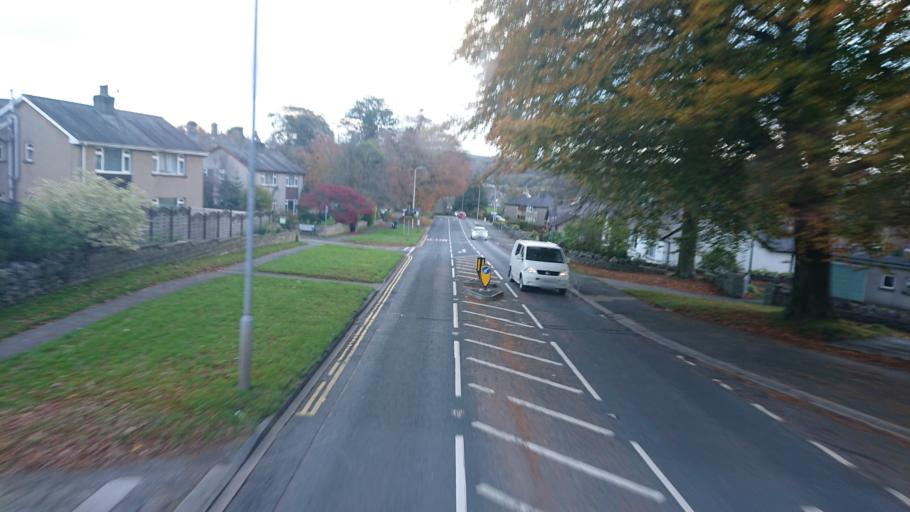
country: GB
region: England
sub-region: Cumbria
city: Kendal
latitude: 54.3141
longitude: -2.7501
